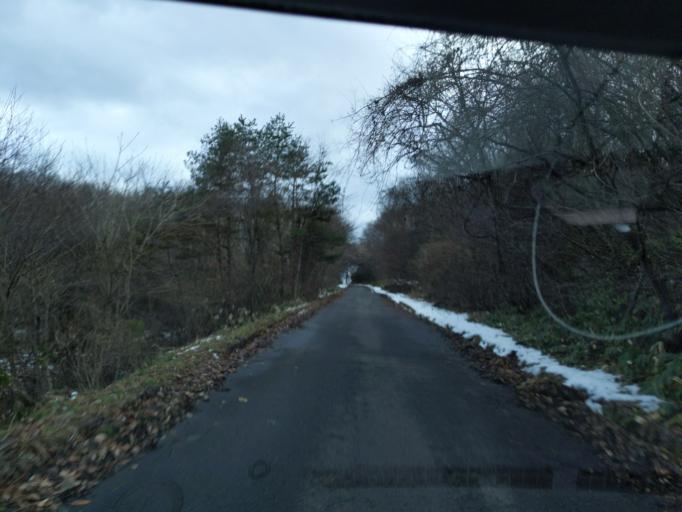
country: JP
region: Iwate
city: Ichinoseki
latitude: 38.9926
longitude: 141.0006
